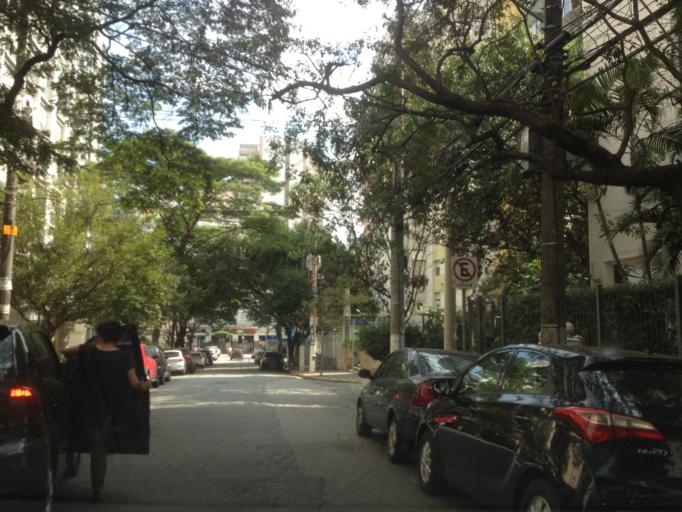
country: BR
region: Sao Paulo
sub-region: Sao Paulo
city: Sao Paulo
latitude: -23.5795
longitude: -46.6738
